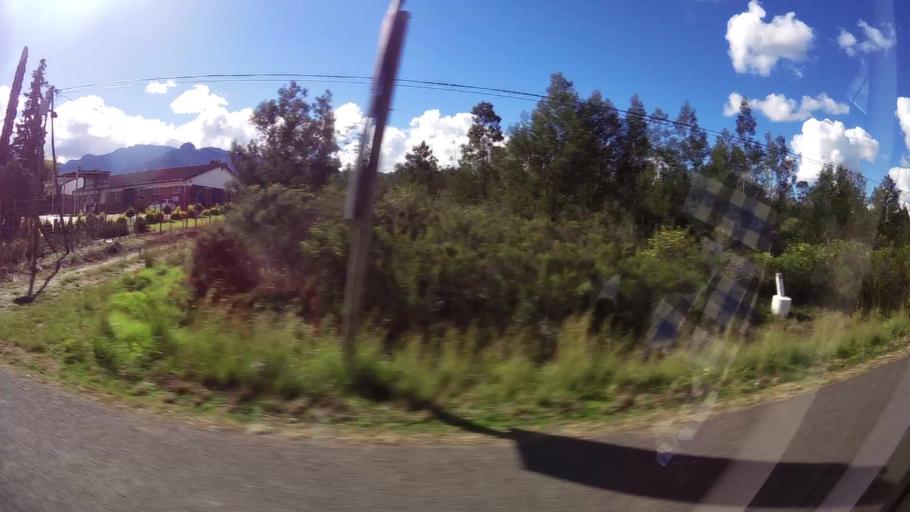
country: ZA
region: Western Cape
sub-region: Overberg District Municipality
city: Swellendam
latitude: -34.0351
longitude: 20.4228
